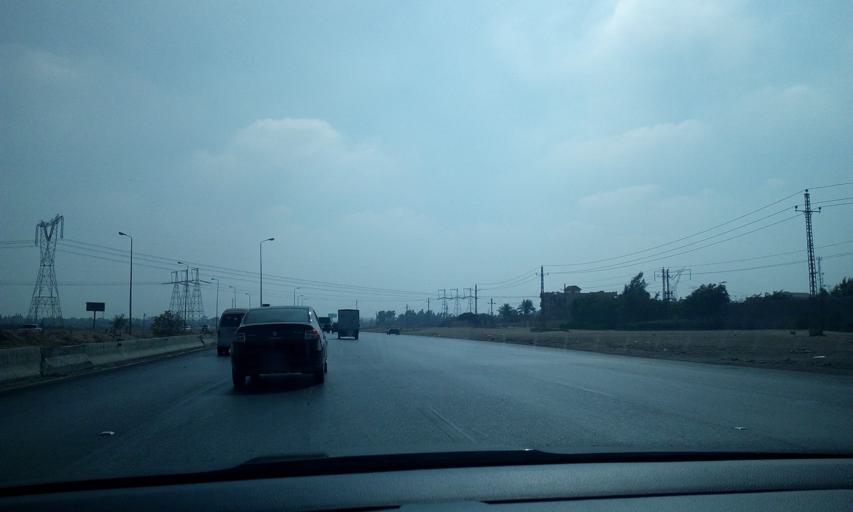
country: EG
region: Eastern Province
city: Bilbays
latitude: 30.1860
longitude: 31.6274
